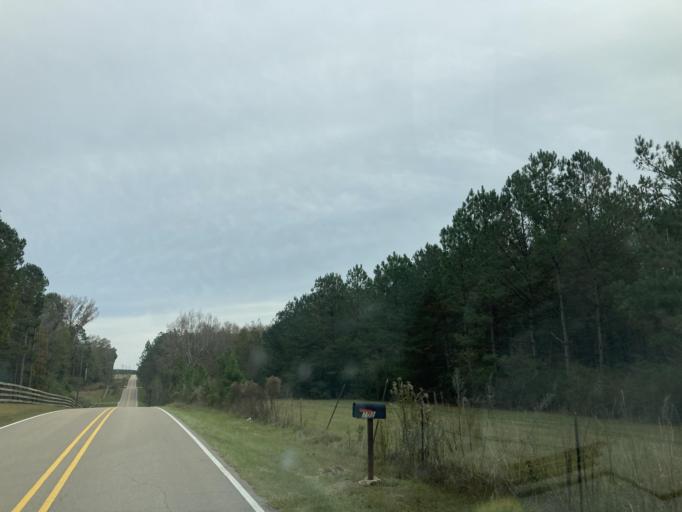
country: US
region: Mississippi
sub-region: Lamar County
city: Lumberton
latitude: 31.0394
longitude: -89.4302
